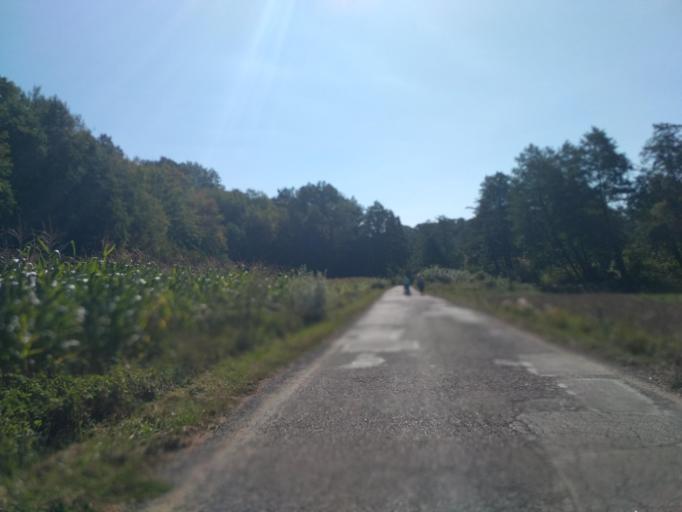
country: PL
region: Subcarpathian Voivodeship
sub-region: Powiat brzozowski
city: Brzozow
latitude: 49.7115
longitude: 22.0402
